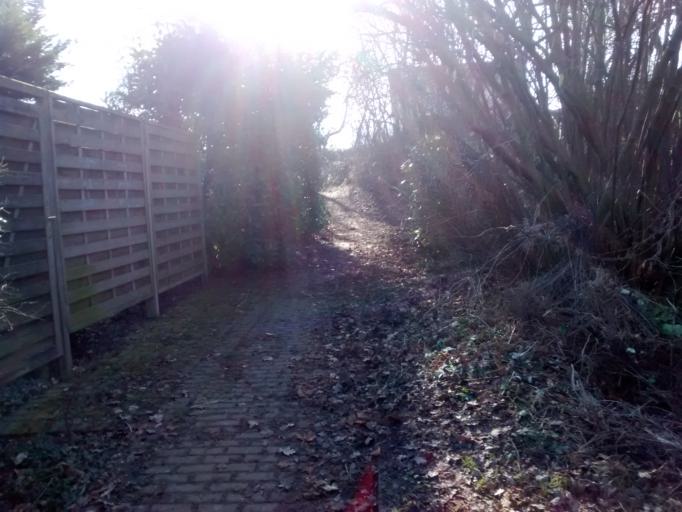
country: NL
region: Limburg
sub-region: Gemeente Vaals
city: Vaals
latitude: 50.7681
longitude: 6.0436
